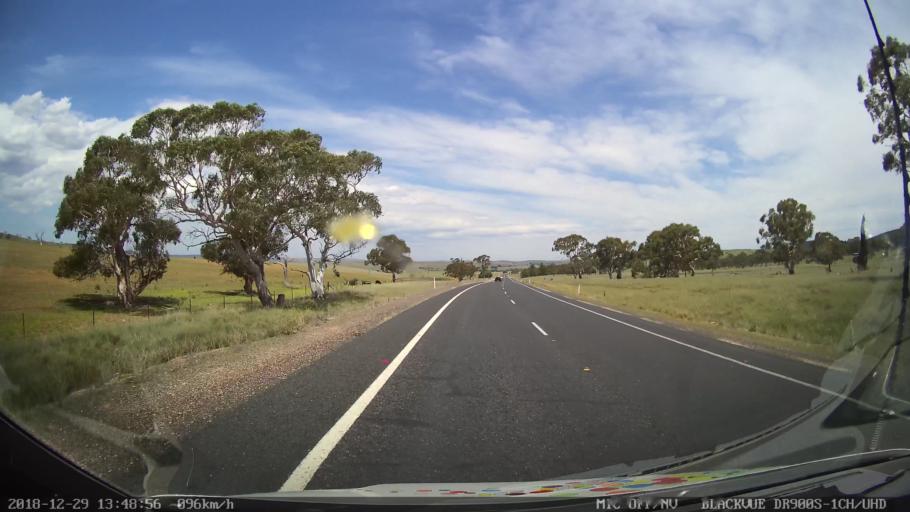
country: AU
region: New South Wales
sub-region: Cooma-Monaro
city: Cooma
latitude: -36.1470
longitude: 149.1499
